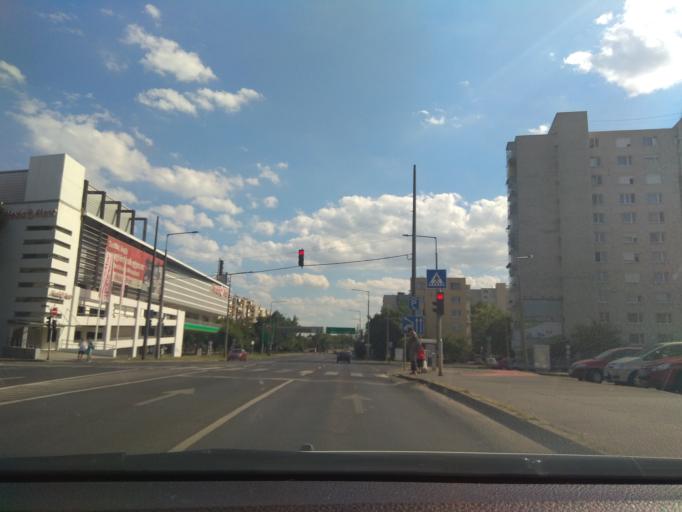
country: HU
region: Borsod-Abauj-Zemplen
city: Miskolc
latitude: 48.1022
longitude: 20.7917
